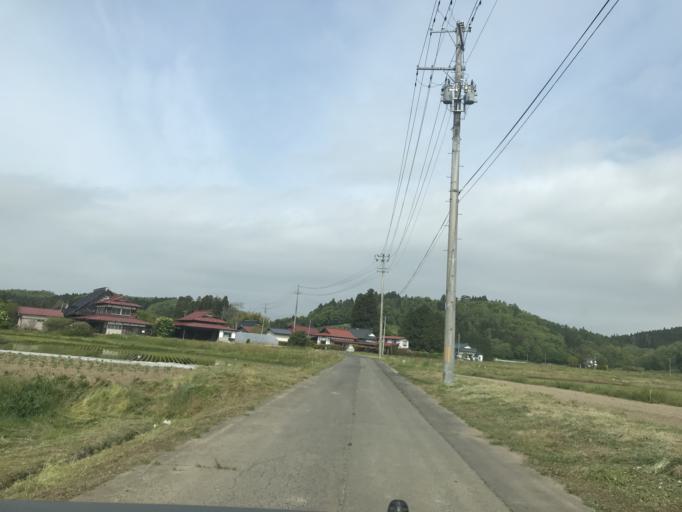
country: JP
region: Iwate
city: Ichinoseki
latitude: 38.9210
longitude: 141.0842
